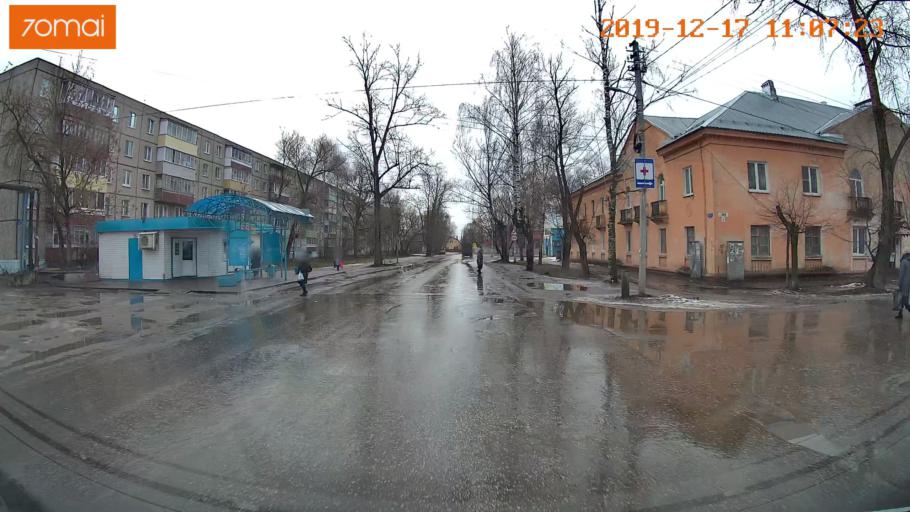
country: RU
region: Vladimir
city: Gus'-Khrustal'nyy
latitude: 55.6110
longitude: 40.6446
